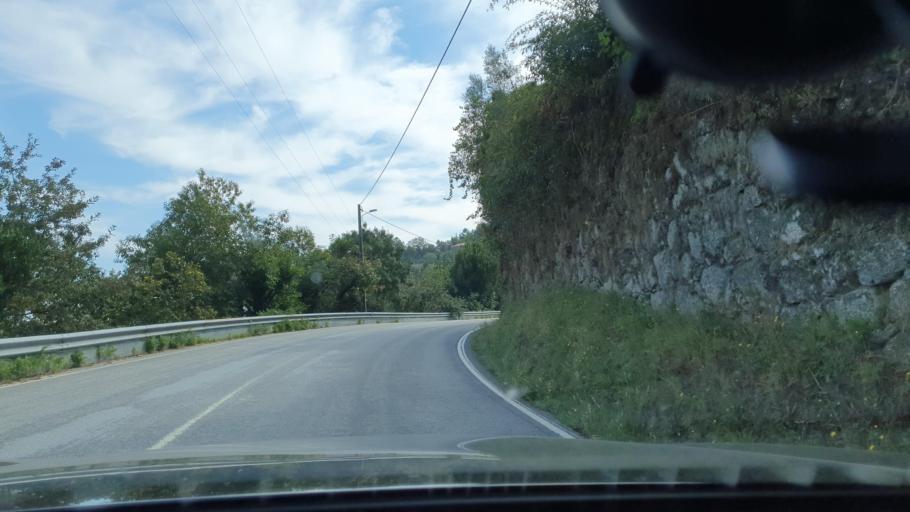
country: PT
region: Braga
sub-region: Vieira do Minho
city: Vieira do Minho
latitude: 41.6800
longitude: -8.1152
